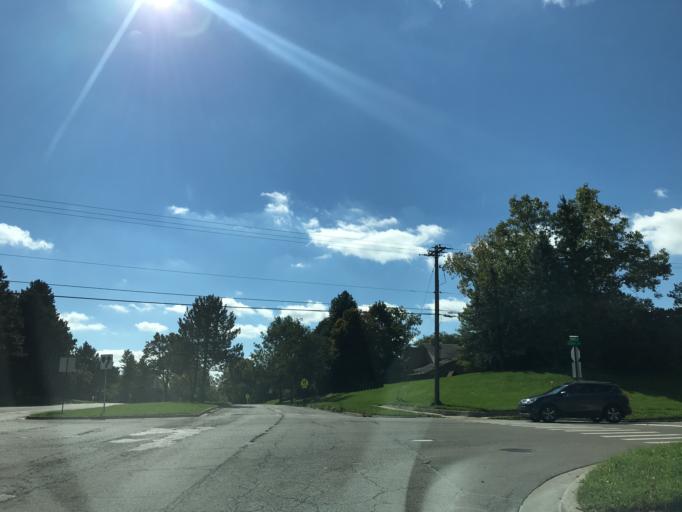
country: US
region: Michigan
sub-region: Washtenaw County
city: Ann Arbor
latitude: 42.2885
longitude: -83.6825
